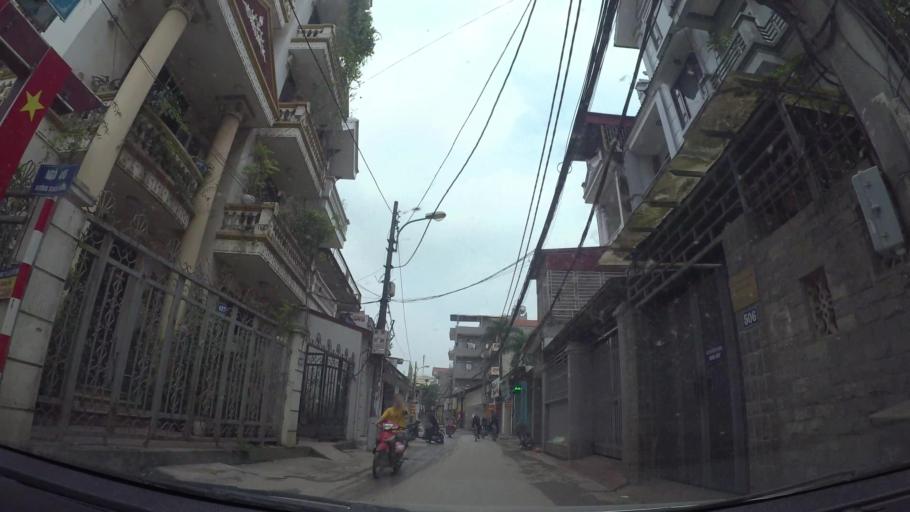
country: VN
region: Ha Noi
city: Tay Ho
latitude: 21.0747
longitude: 105.7886
